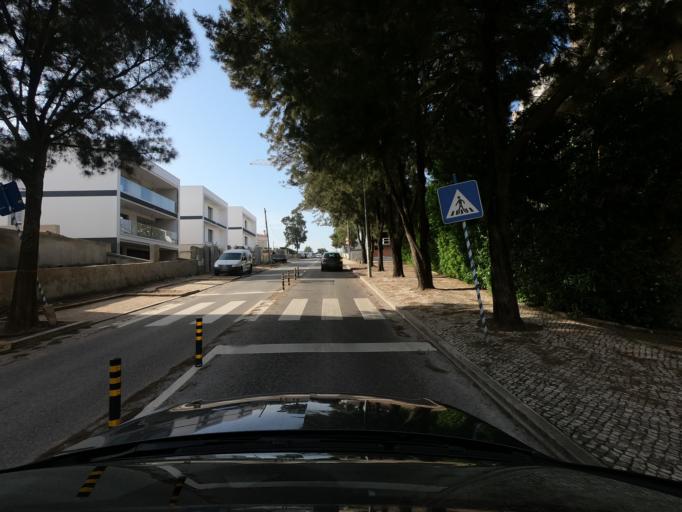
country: PT
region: Lisbon
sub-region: Oeiras
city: Oeiras
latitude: 38.6844
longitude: -9.3152
